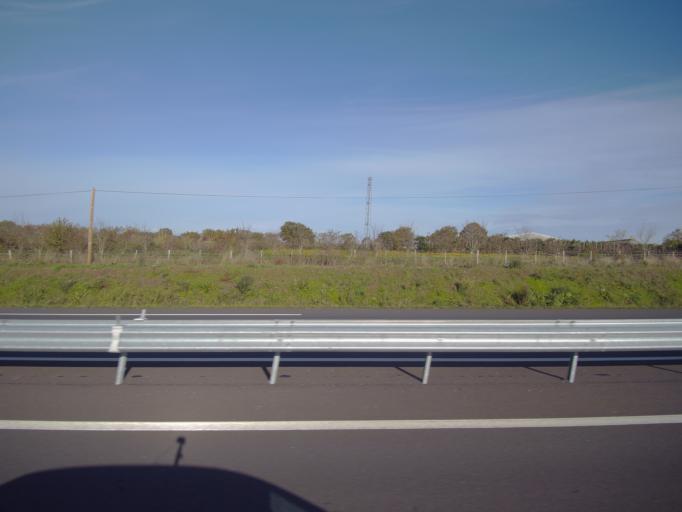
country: FR
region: Pays de la Loire
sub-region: Departement de Maine-et-Loire
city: Coron
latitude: 47.1335
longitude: -0.5964
